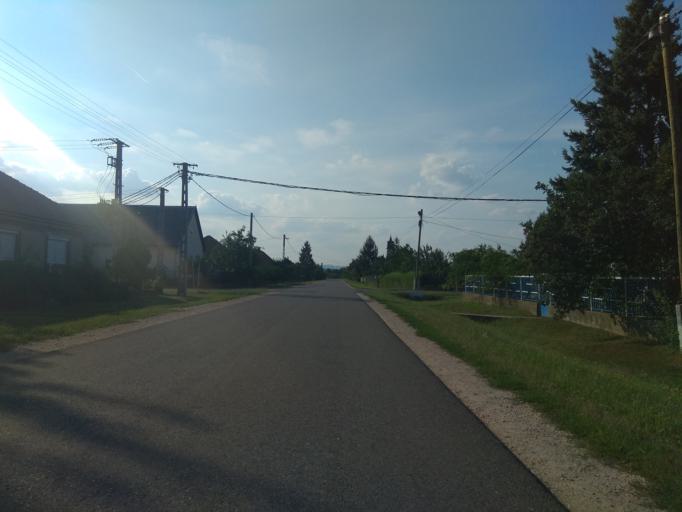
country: HU
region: Borsod-Abauj-Zemplen
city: Emod
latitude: 47.8875
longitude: 20.7673
